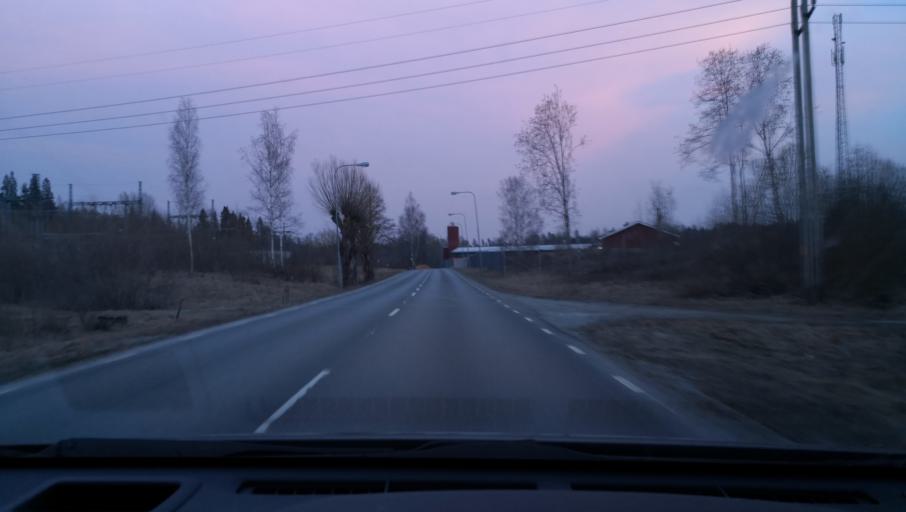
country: SE
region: OErebro
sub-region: Lindesbergs Kommun
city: Lindesberg
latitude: 59.5903
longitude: 15.2480
